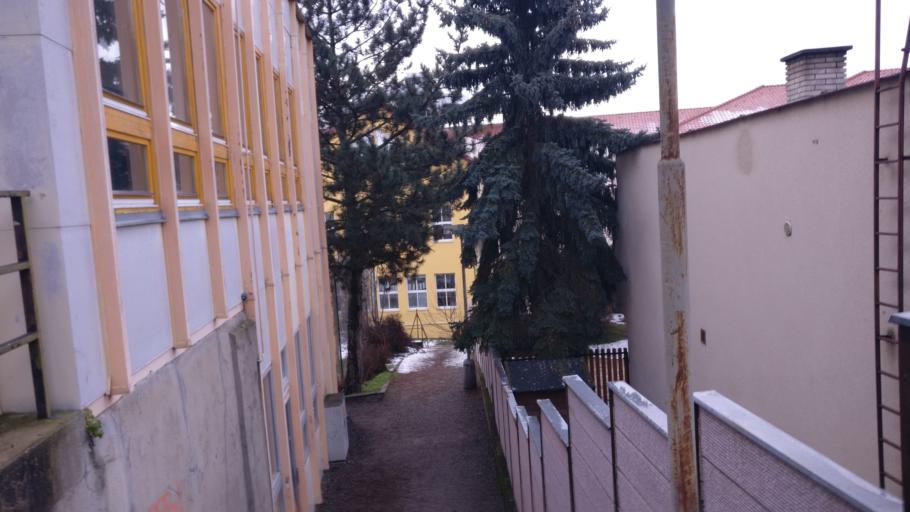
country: CZ
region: South Moravian
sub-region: Okres Brno-Venkov
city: Rosice
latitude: 49.1809
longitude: 16.3897
